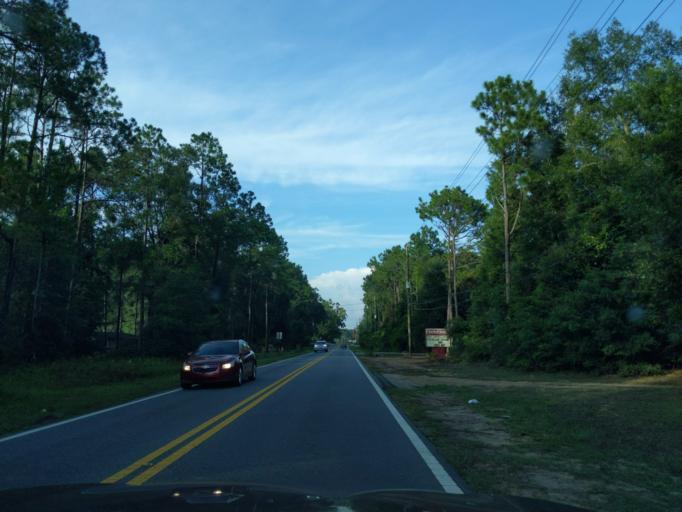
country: US
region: Florida
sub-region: Leon County
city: Tallahassee
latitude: 30.4002
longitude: -84.3131
